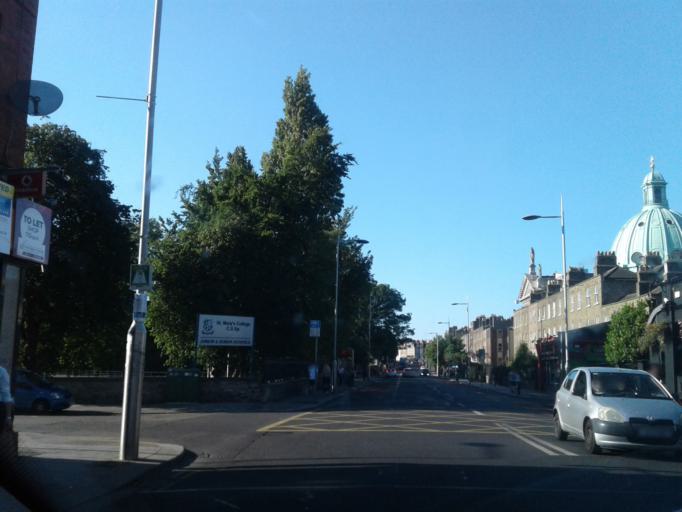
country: IE
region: Leinster
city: Rathmines
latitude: 53.3267
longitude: -6.2649
